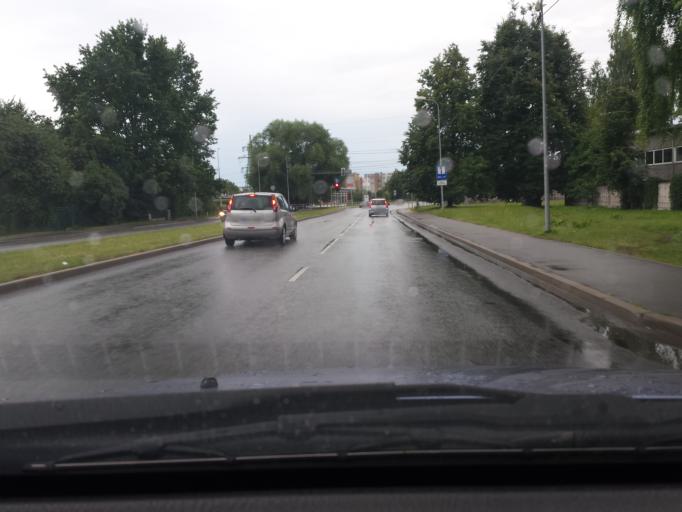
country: LV
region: Riga
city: Riga
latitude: 56.9360
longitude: 24.1823
